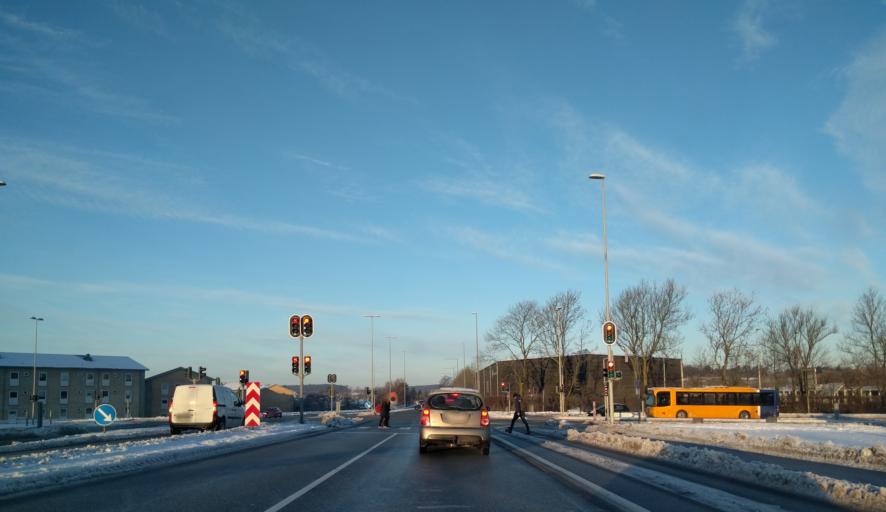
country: DK
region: North Denmark
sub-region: Alborg Kommune
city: Aalborg
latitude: 57.0242
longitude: 9.9431
